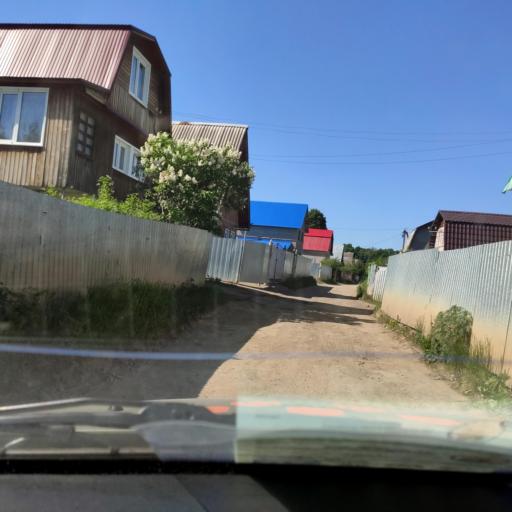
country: RU
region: Bashkortostan
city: Ufa
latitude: 54.7871
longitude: 56.1839
